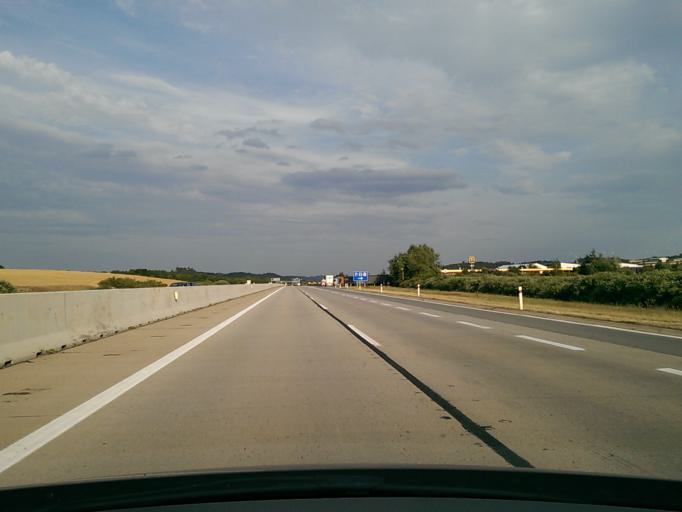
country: CZ
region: Vysocina
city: Merin
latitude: 49.3796
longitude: 15.9430
